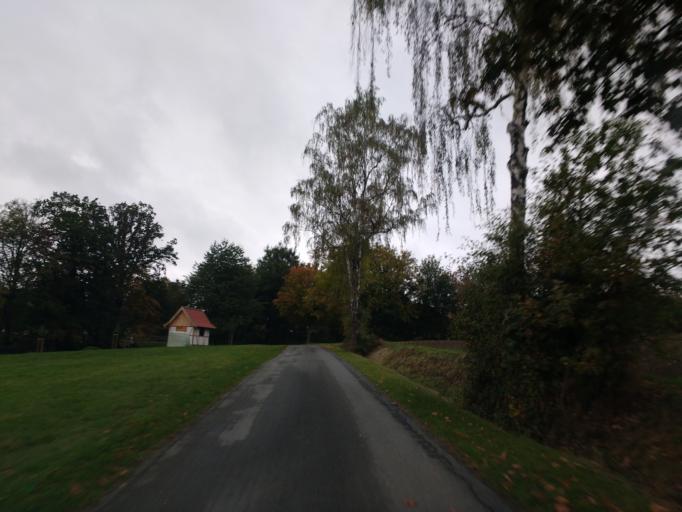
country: DE
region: North Rhine-Westphalia
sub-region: Regierungsbezirk Detmold
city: Lemgo
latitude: 51.9914
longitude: 8.9462
